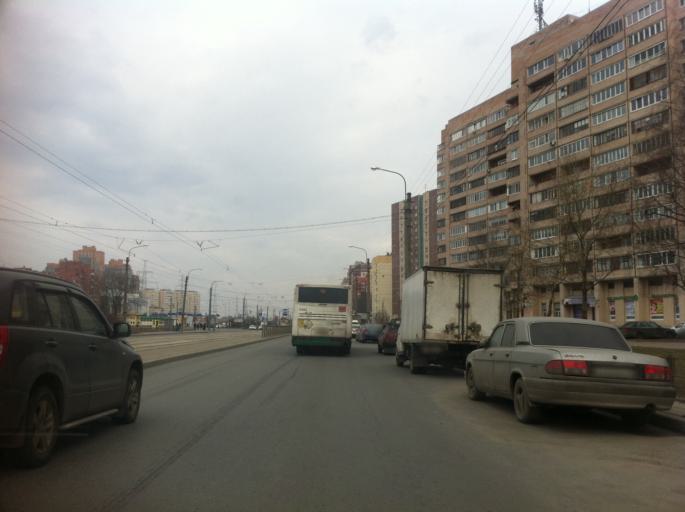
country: RU
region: St.-Petersburg
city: Uritsk
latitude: 59.8508
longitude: 30.1981
